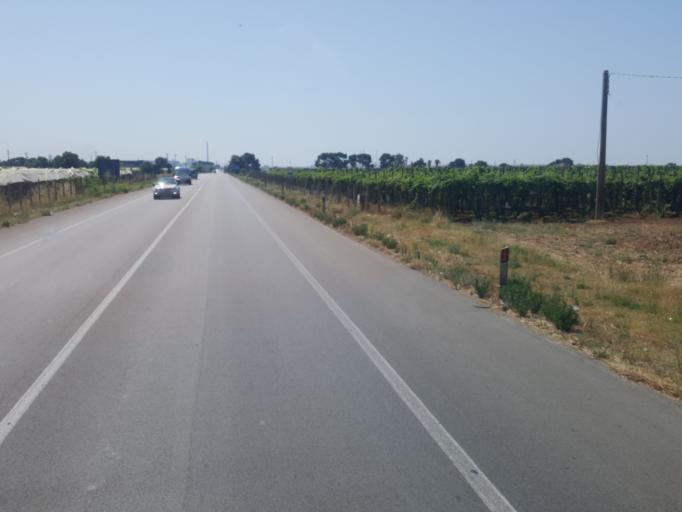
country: IT
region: Apulia
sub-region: Provincia di Taranto
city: Statte
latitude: 40.5341
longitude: 17.1625
